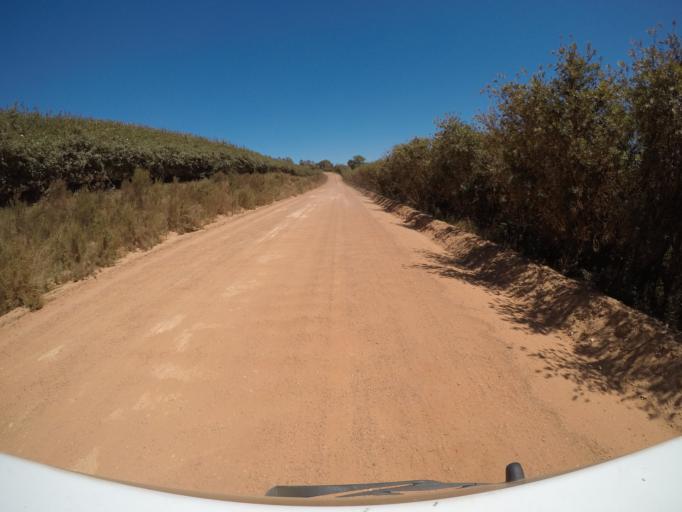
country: ZA
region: Western Cape
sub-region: Overberg District Municipality
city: Grabouw
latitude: -34.2378
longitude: 19.0814
